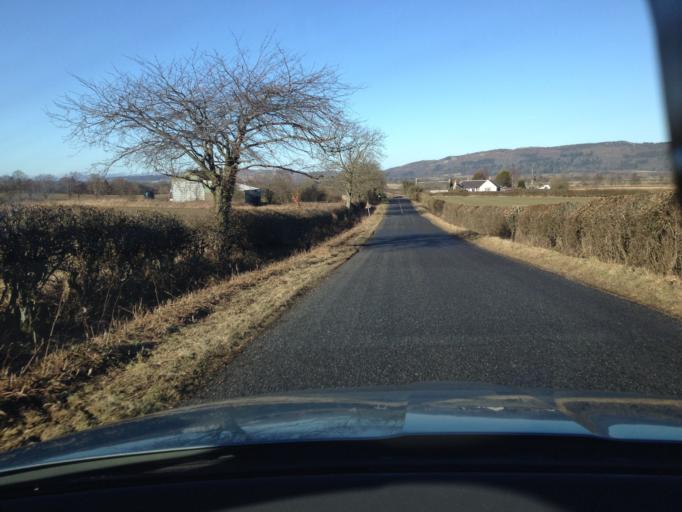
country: GB
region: Scotland
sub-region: Perth and Kinross
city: Bridge of Earn
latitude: 56.3242
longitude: -3.3755
